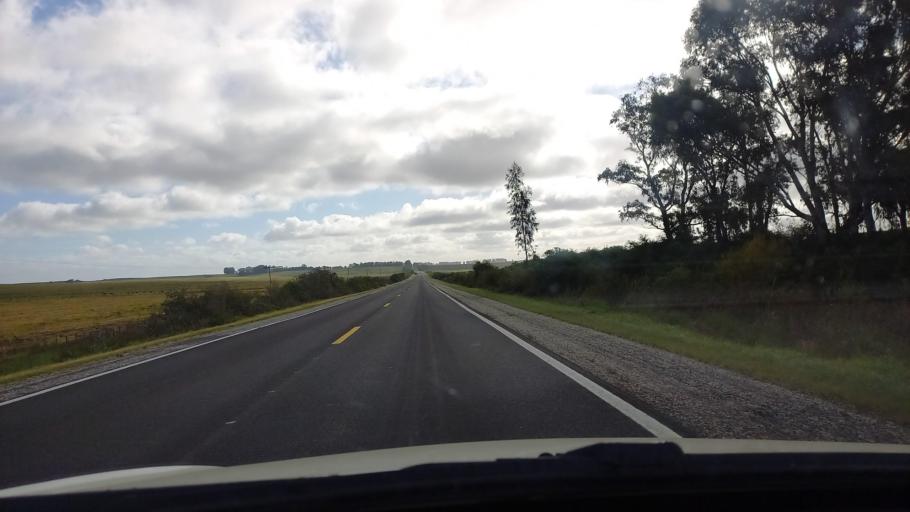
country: BR
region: Rio Grande do Sul
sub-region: Dom Pedrito
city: Dom Pedrito
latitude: -30.8906
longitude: -54.8610
